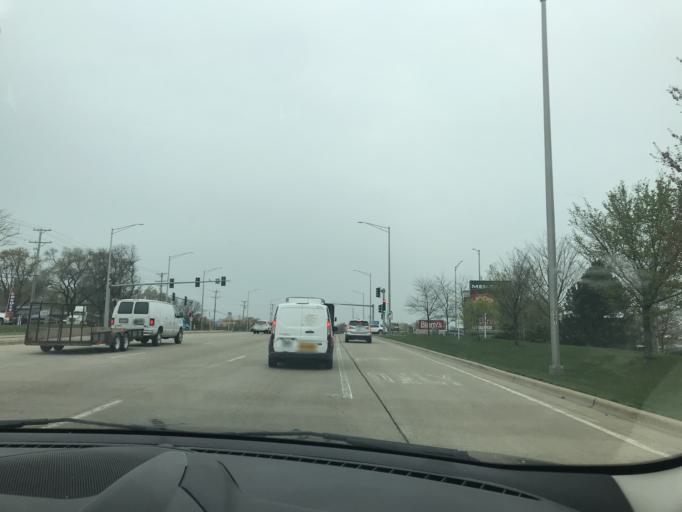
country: US
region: Illinois
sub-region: Kendall County
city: Boulder Hill
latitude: 41.7175
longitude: -88.2838
